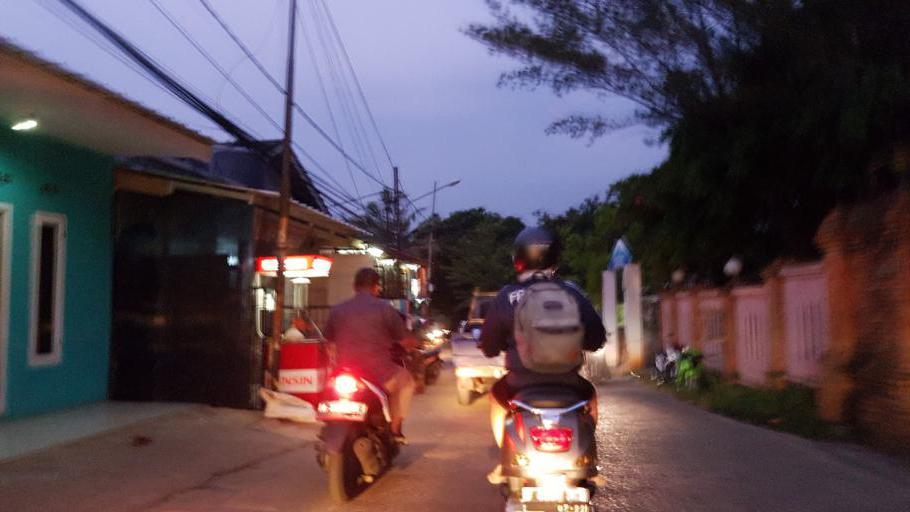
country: ID
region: West Java
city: Pamulang
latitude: -6.3393
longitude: 106.7889
